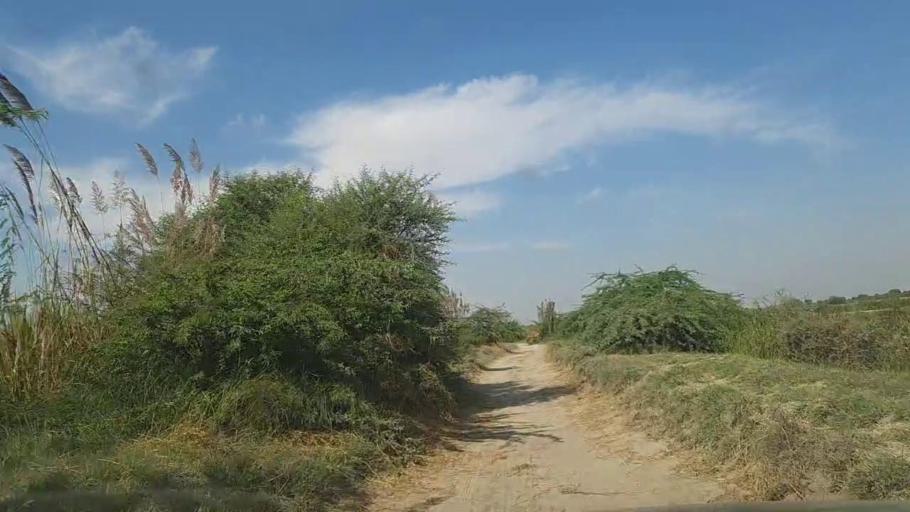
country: PK
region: Sindh
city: Bulri
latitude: 24.8146
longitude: 68.2657
